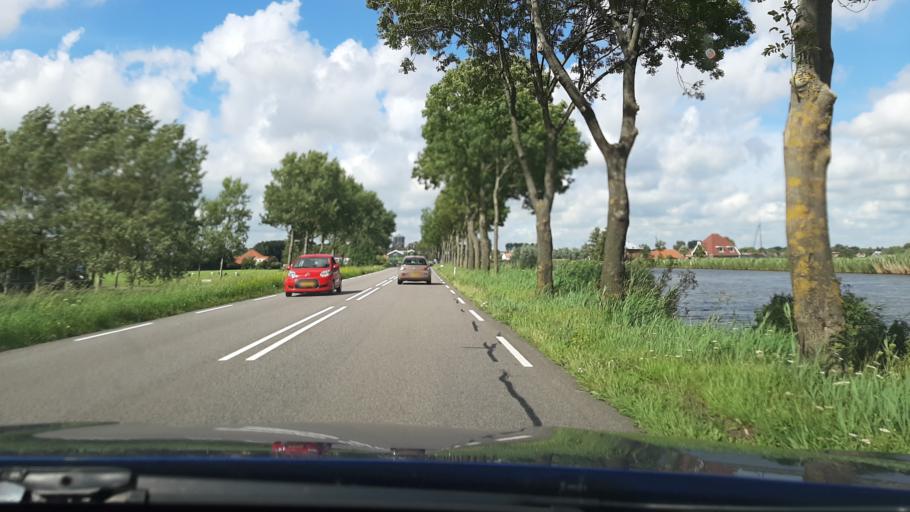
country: NL
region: North Holland
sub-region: Gemeente Zaanstad
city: Zaanstad
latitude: 52.4557
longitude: 4.7601
